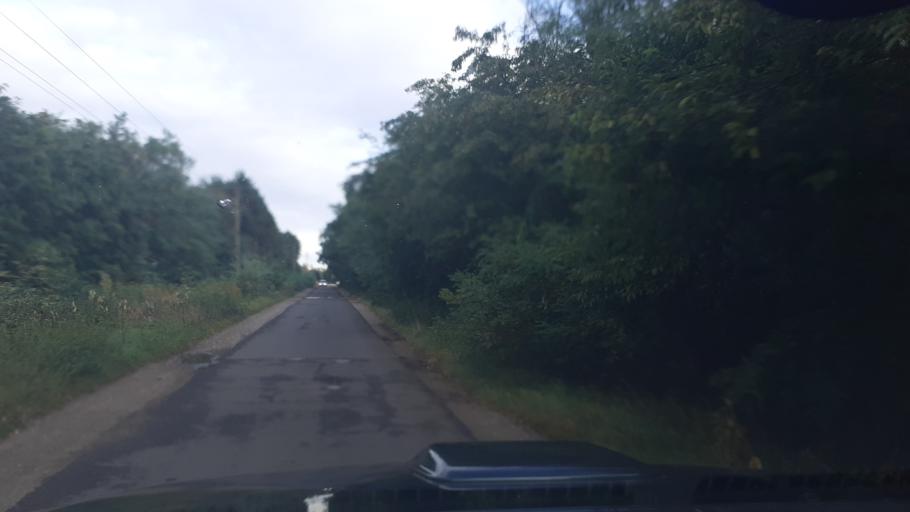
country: HU
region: Fejer
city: dunaujvaros
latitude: 46.9470
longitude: 18.8609
